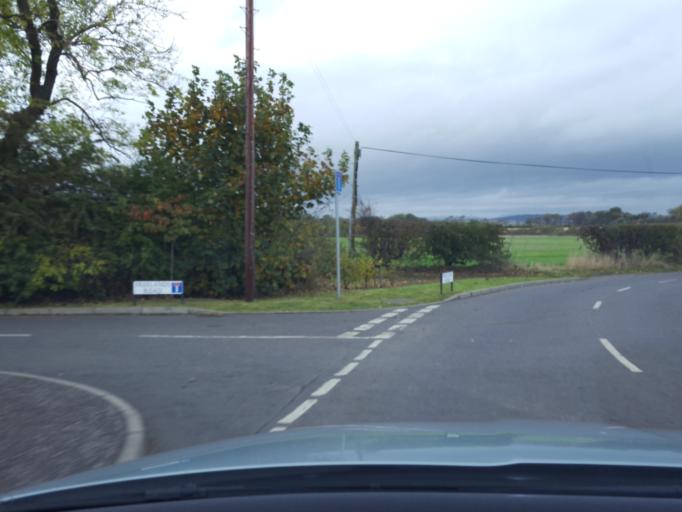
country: GB
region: Scotland
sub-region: Edinburgh
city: Ratho
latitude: 55.9260
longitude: -3.3748
